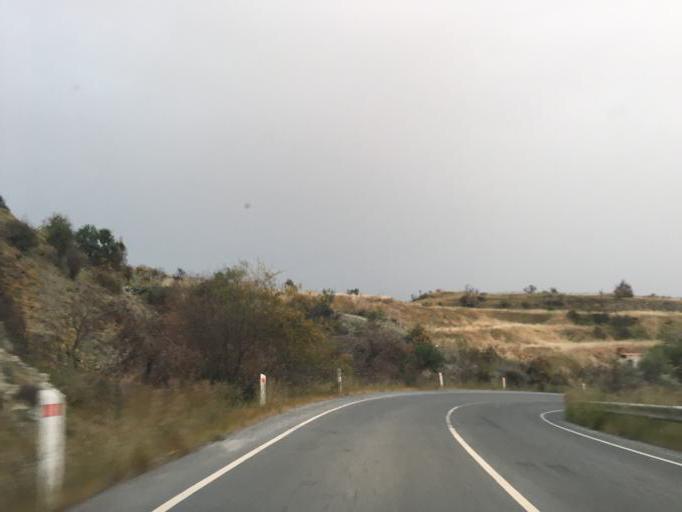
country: CY
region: Limassol
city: Parekklisha
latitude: 34.7852
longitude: 33.1646
